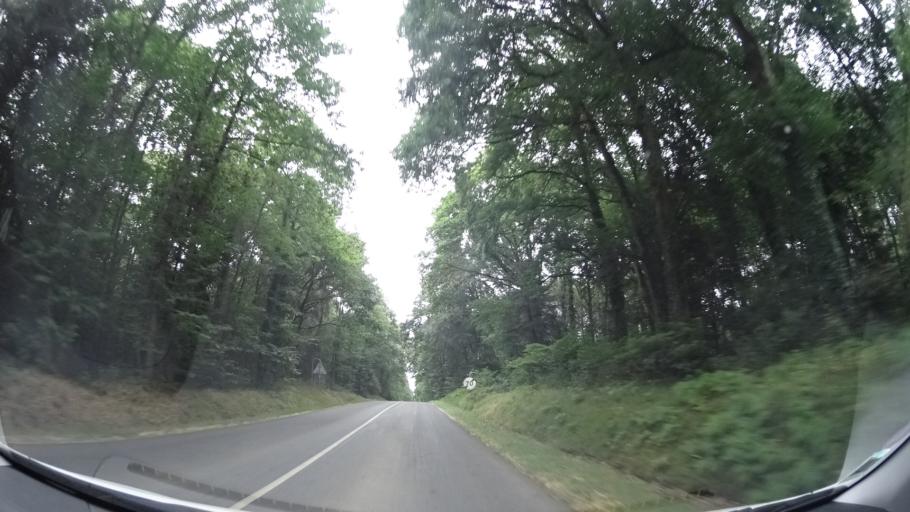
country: FR
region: Brittany
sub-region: Departement d'Ille-et-Vilaine
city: Pleugueneuc
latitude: 48.3514
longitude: -1.9246
